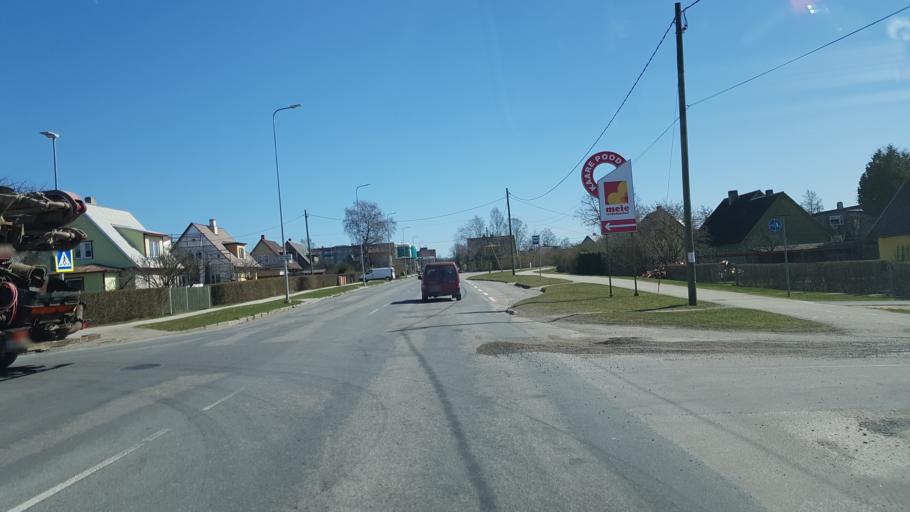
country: EE
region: Viljandimaa
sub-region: Viljandi linn
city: Viljandi
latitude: 58.3711
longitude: 25.5746
